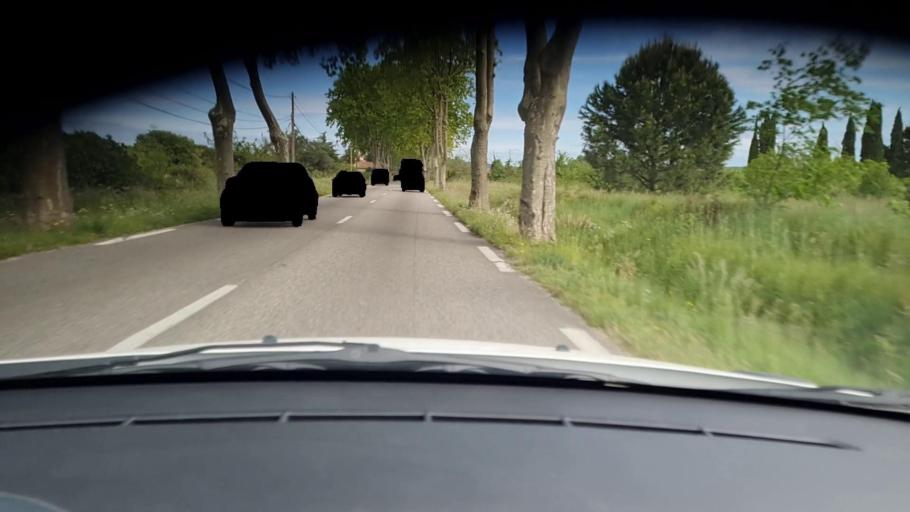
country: FR
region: Languedoc-Roussillon
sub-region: Departement du Gard
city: Remoulins
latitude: 43.9479
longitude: 4.5697
